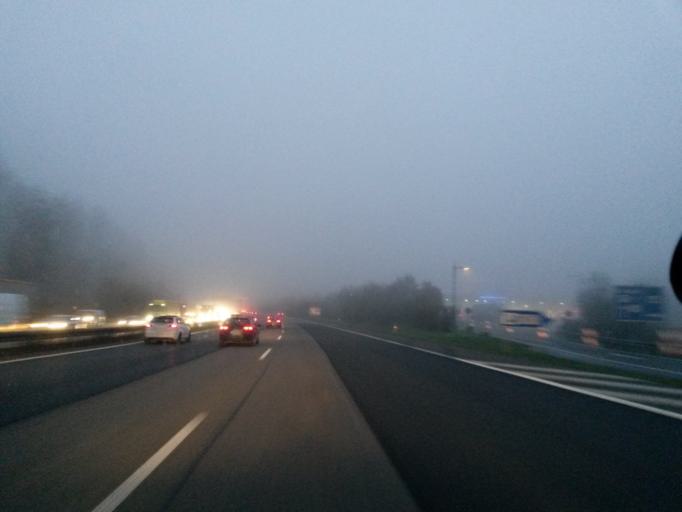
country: DE
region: Baden-Wuerttemberg
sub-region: Regierungsbezirk Stuttgart
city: Sindelfingen
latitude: 48.7442
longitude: 9.0346
